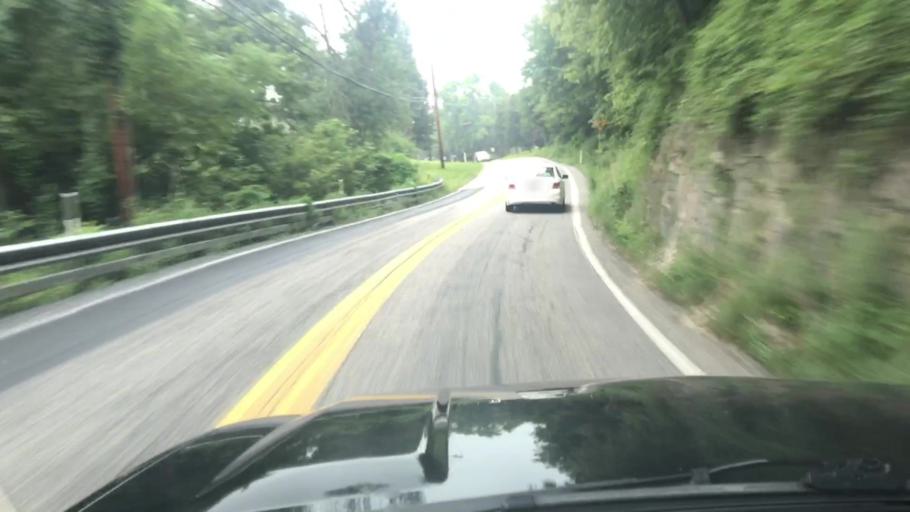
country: US
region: Pennsylvania
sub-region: Cumberland County
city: Shiremanstown
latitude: 40.2642
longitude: -76.9783
